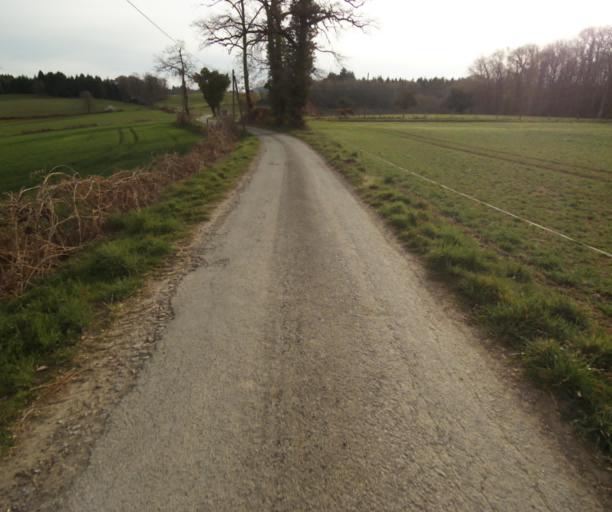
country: FR
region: Limousin
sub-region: Departement de la Correze
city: Chamboulive
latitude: 45.4618
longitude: 1.7621
